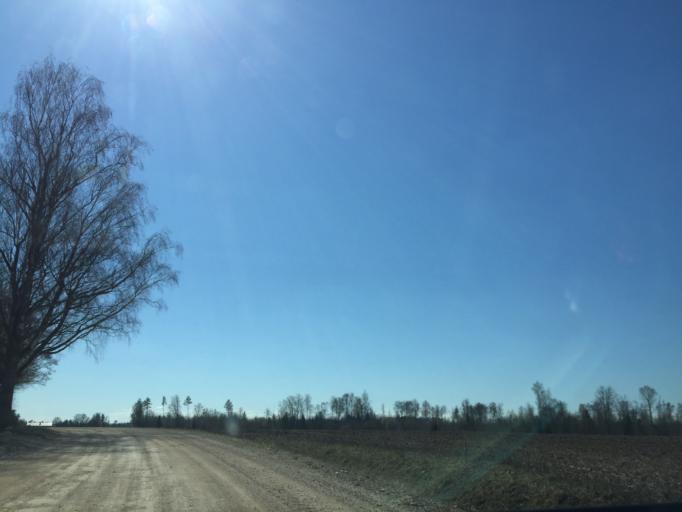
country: EE
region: Viljandimaa
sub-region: Viiratsi vald
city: Viiratsi
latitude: 58.3562
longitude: 25.7220
